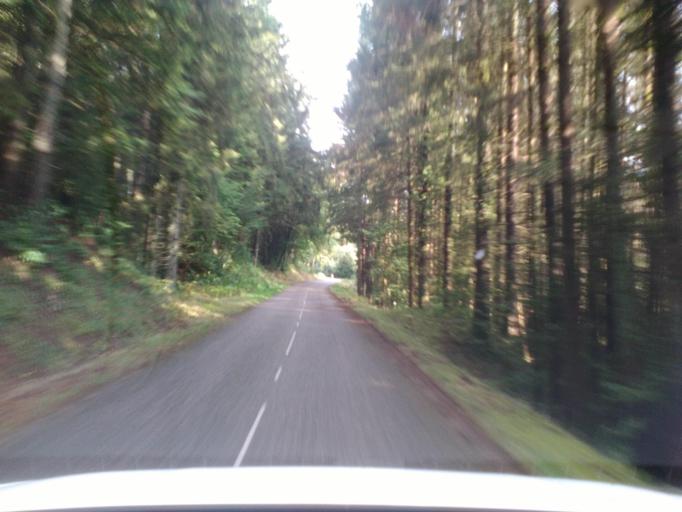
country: FR
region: Lorraine
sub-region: Departement des Vosges
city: Senones
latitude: 48.3870
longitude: 7.0334
